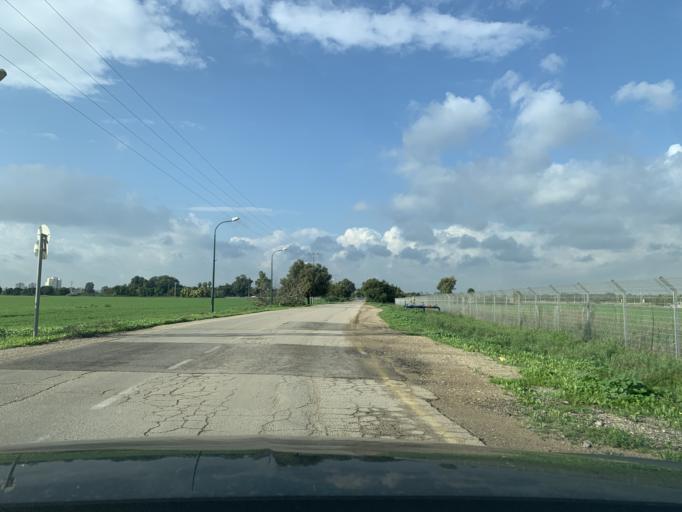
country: IL
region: Central District
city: Petah Tiqwa
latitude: 32.0955
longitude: 34.9183
